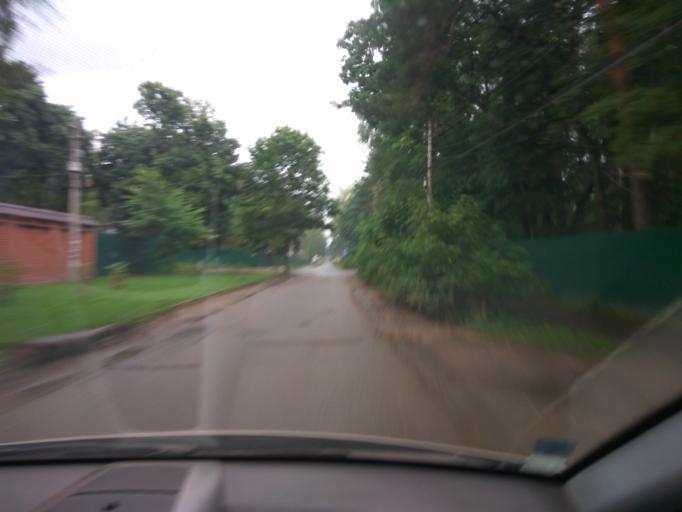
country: RU
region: Moskovskaya
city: Rodniki
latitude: 55.6331
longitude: 38.0603
